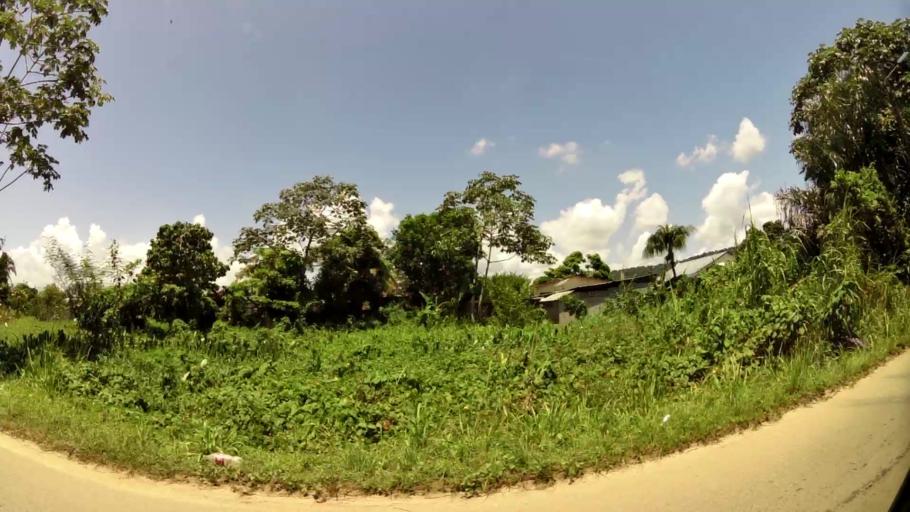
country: GF
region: Guyane
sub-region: Guyane
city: Matoury
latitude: 4.8863
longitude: -52.3399
